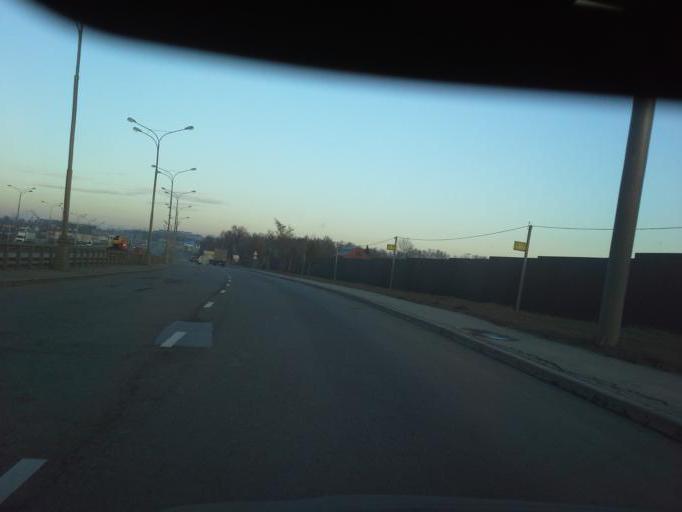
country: RU
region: Moscow
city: Vnukovo
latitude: 55.5895
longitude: 37.2233
